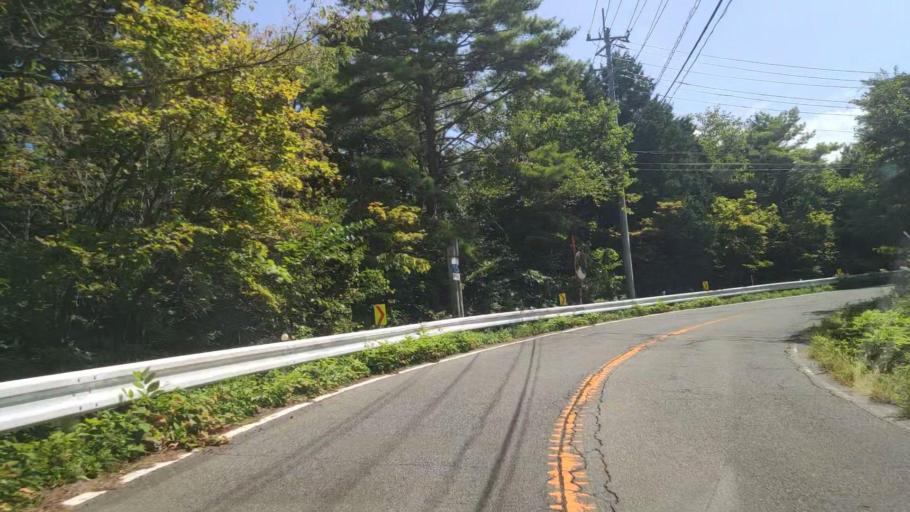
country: JP
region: Gunma
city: Shibukawa
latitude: 36.4958
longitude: 138.9059
